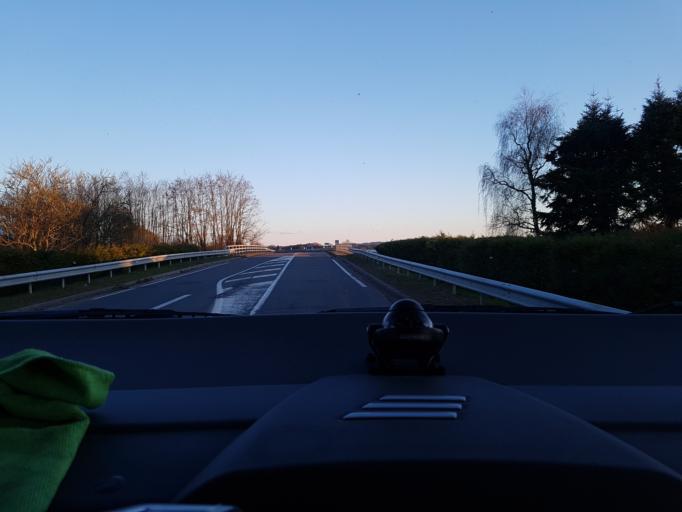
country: FR
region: Bourgogne
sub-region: Departement de Saone-et-Loire
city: Etang-sur-Arroux
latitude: 46.8695
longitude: 4.1755
